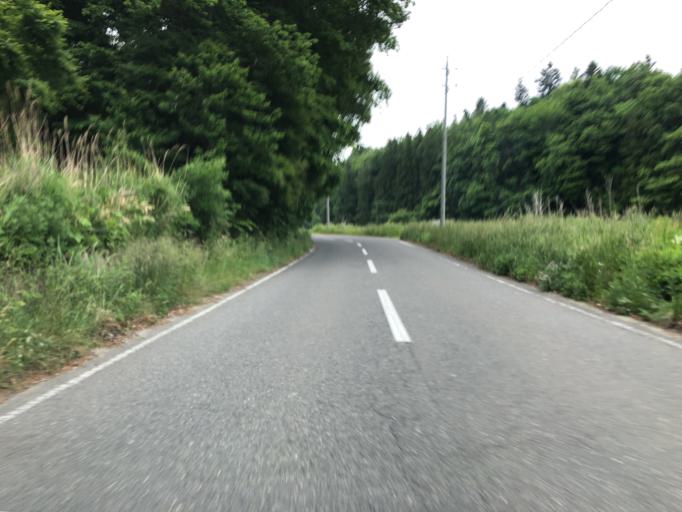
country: JP
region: Fukushima
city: Funehikimachi-funehiki
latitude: 37.4257
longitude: 140.6180
